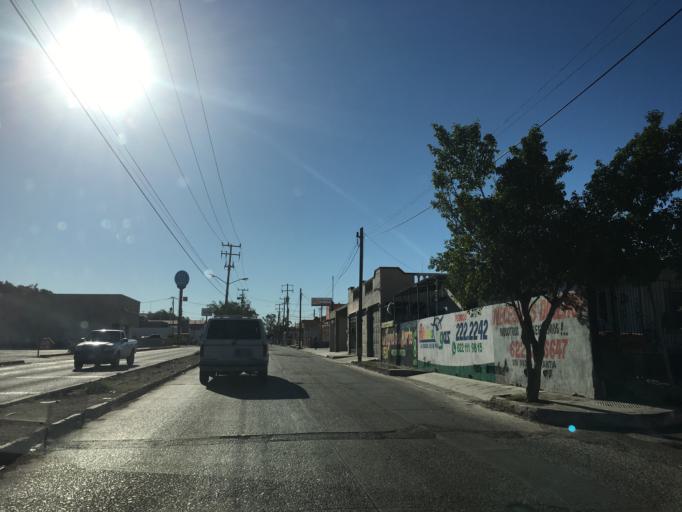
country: MX
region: Sonora
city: Heroica Guaymas
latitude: 27.9206
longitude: -110.9161
